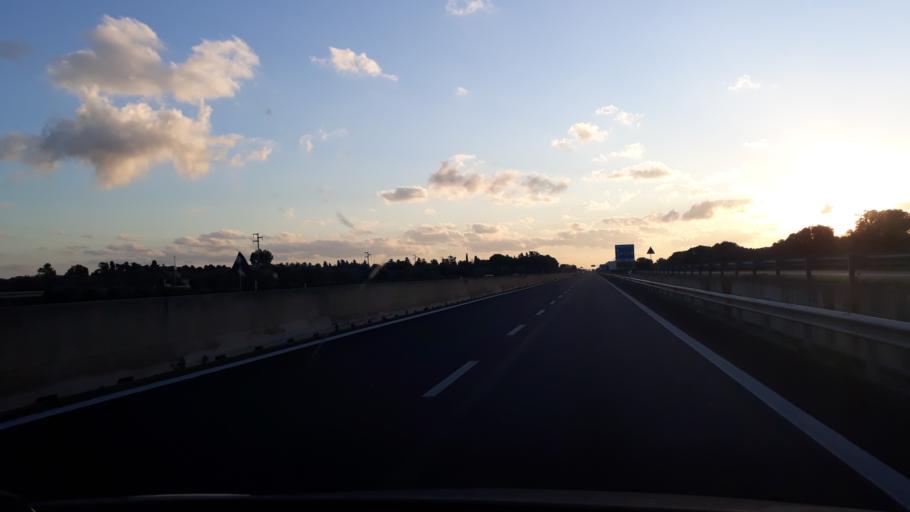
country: IT
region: Apulia
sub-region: Provincia di Brindisi
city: Ostuni
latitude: 40.7672
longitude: 17.6292
